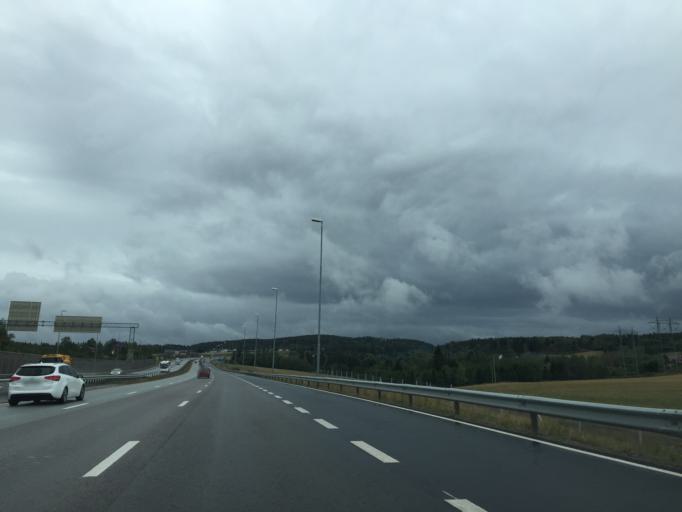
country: NO
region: Akershus
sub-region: Lorenskog
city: Kjenn
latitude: 59.9760
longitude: 10.9919
